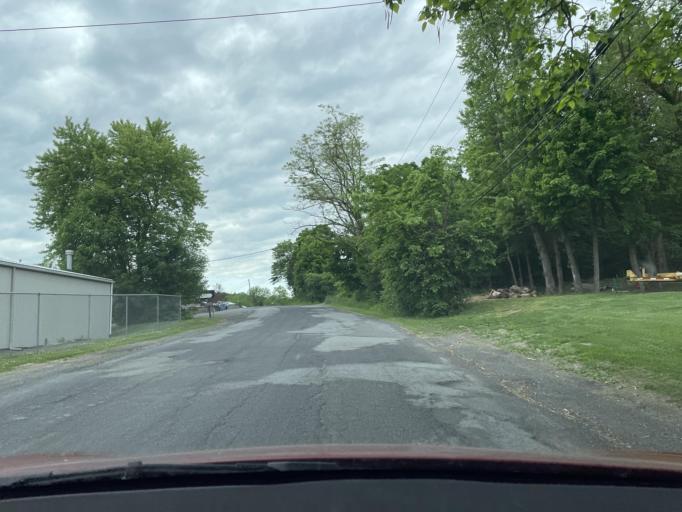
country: US
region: New York
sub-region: Ulster County
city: Saugerties
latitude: 42.0816
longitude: -73.9598
